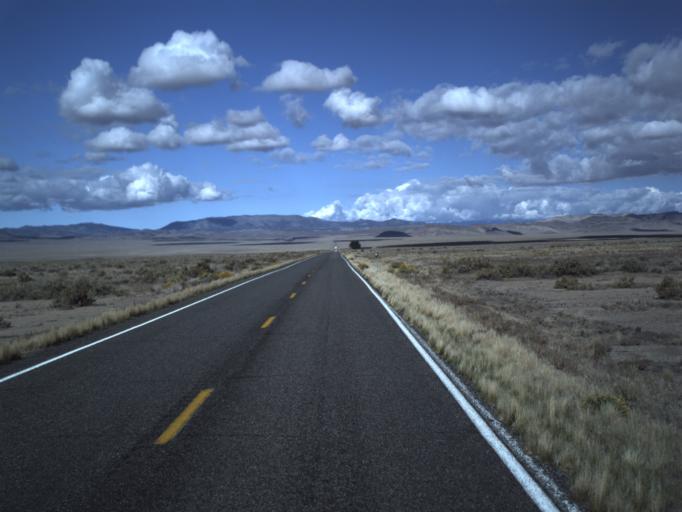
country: US
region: Utah
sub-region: Beaver County
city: Milford
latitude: 38.5300
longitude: -113.6755
